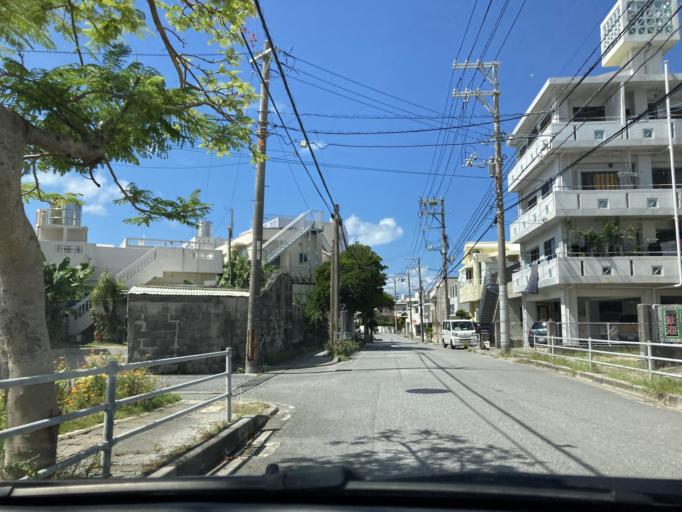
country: JP
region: Okinawa
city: Tomigusuku
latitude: 26.1938
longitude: 127.6694
